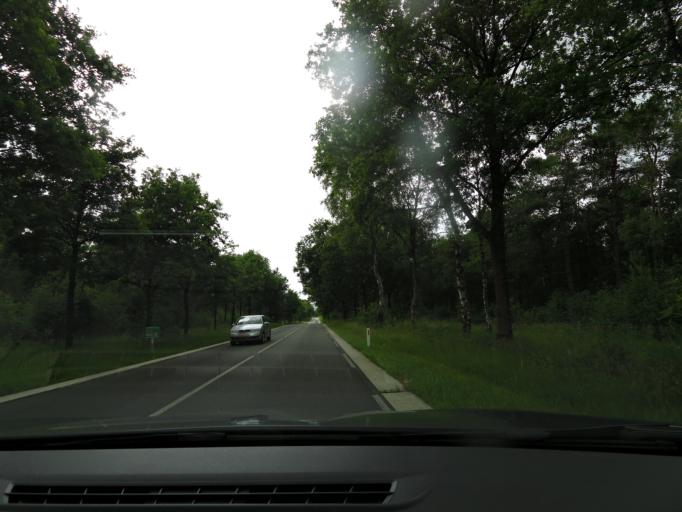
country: NL
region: Gelderland
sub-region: Gemeente Barneveld
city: Garderen
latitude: 52.2417
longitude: 5.7387
